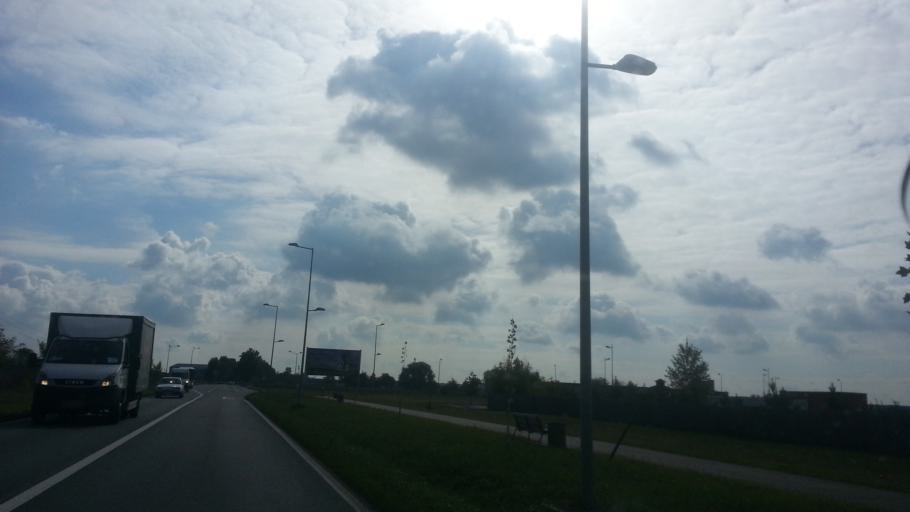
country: RS
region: Autonomna Pokrajina Vojvodina
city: Nova Pazova
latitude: 44.9581
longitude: 20.1984
